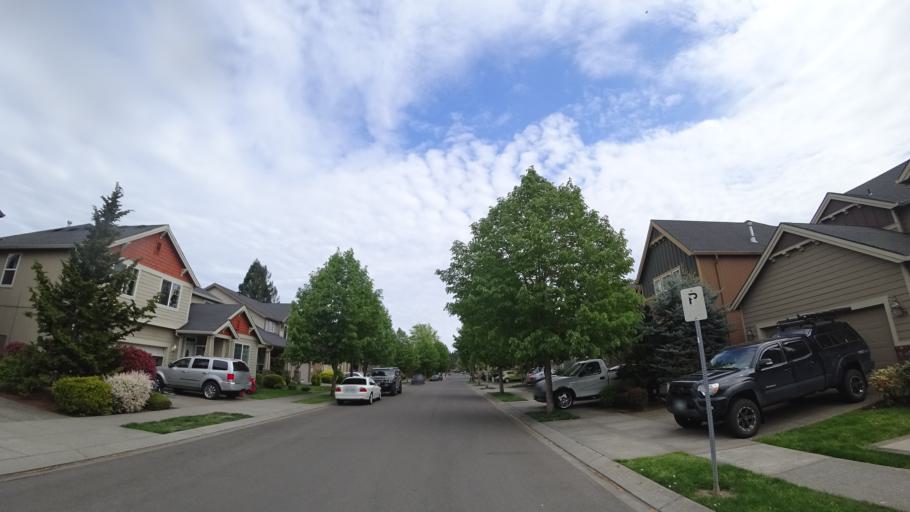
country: US
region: Oregon
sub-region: Washington County
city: Hillsboro
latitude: 45.4950
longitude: -122.9650
